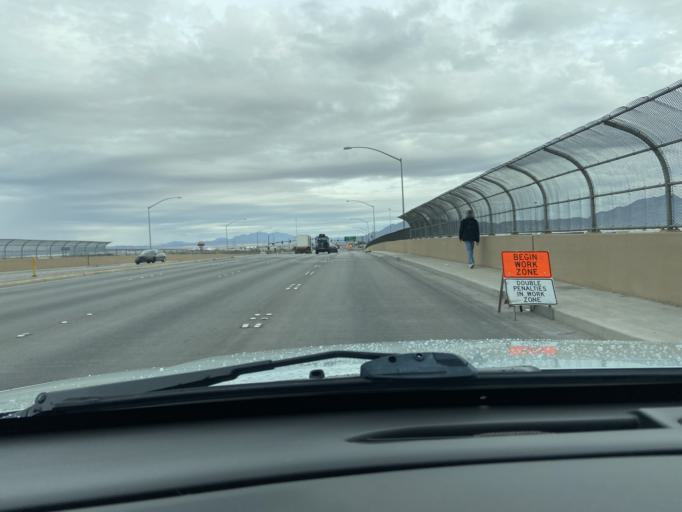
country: US
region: Nevada
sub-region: Clark County
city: North Las Vegas
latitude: 36.2400
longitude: -115.1075
